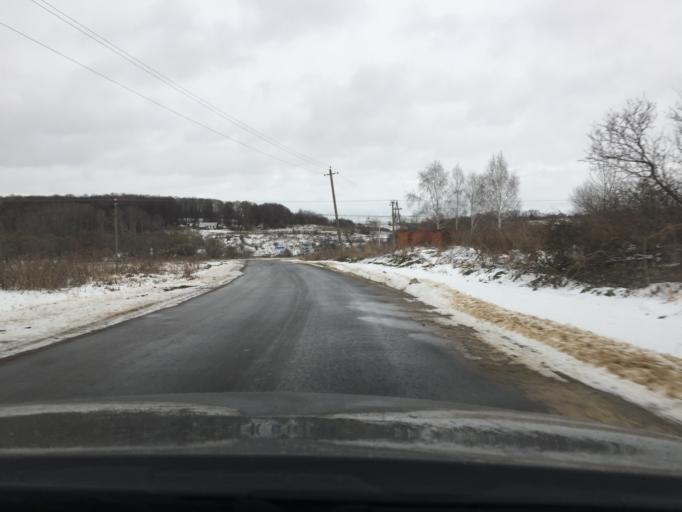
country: RU
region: Tula
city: Shchekino
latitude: 53.8153
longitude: 37.5578
